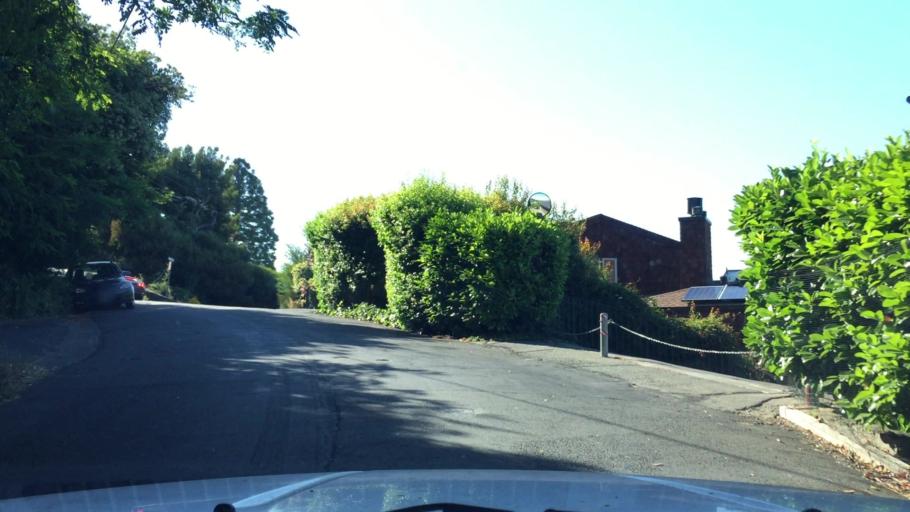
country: US
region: California
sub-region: Marin County
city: Sausalito
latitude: 37.8574
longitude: -122.4907
